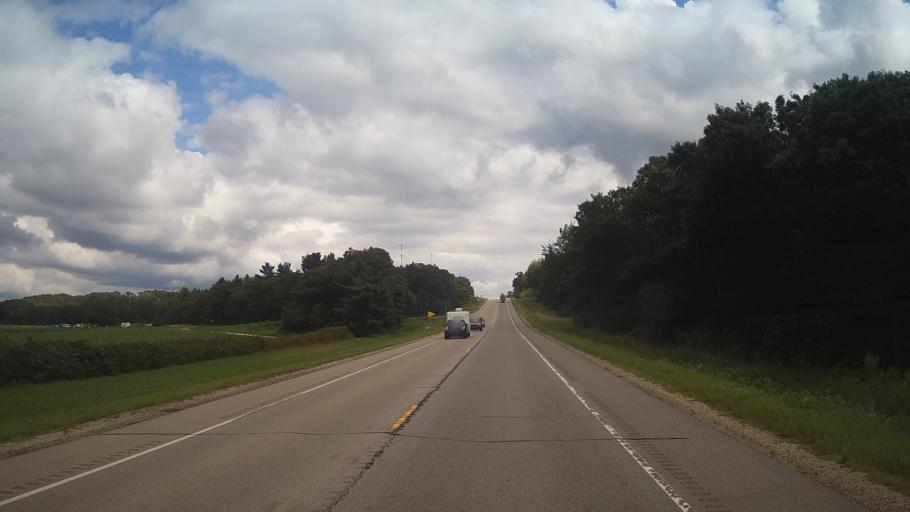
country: US
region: Wisconsin
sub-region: Marquette County
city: Westfield
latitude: 44.0219
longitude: -89.5772
